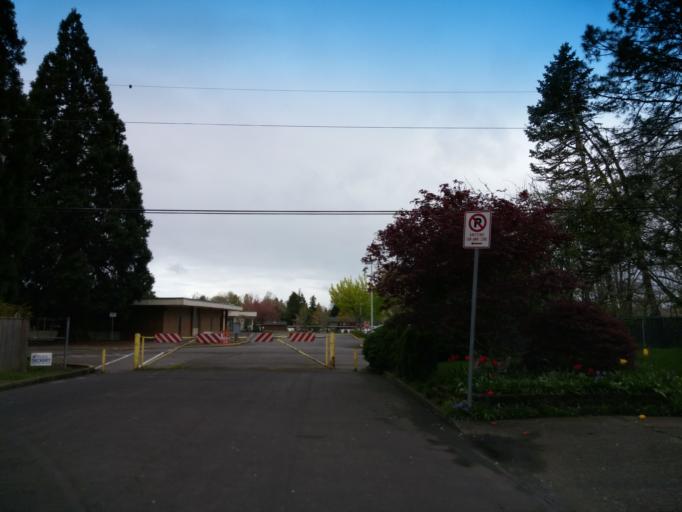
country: US
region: Oregon
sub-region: Washington County
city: Cedar Mill
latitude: 45.5339
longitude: -122.8191
